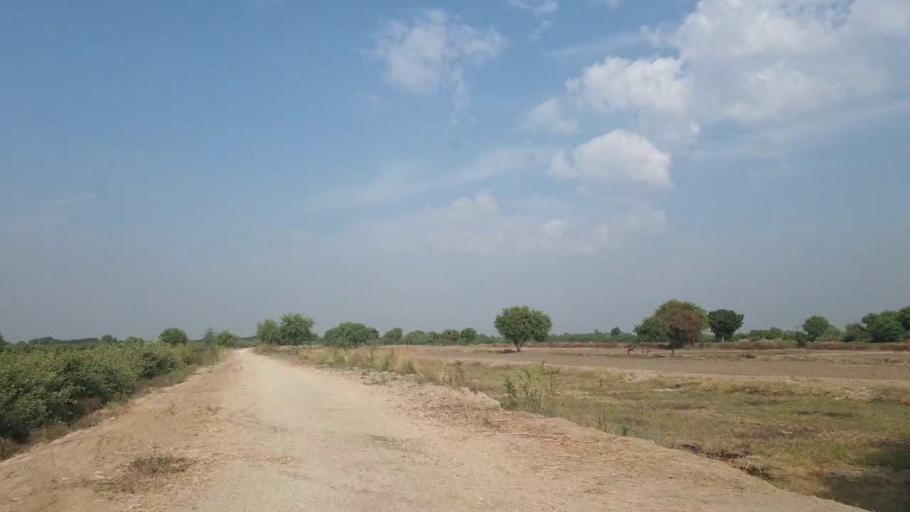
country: PK
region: Sindh
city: Digri
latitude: 25.0144
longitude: 69.0668
